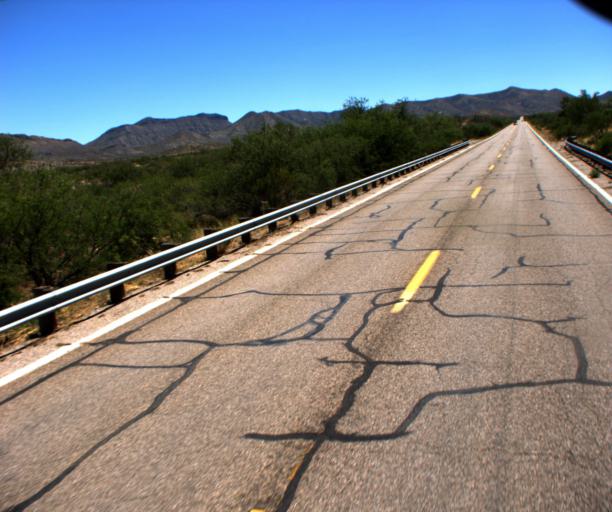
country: US
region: Arizona
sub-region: Pima County
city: Vail
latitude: 31.9526
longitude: -110.6677
